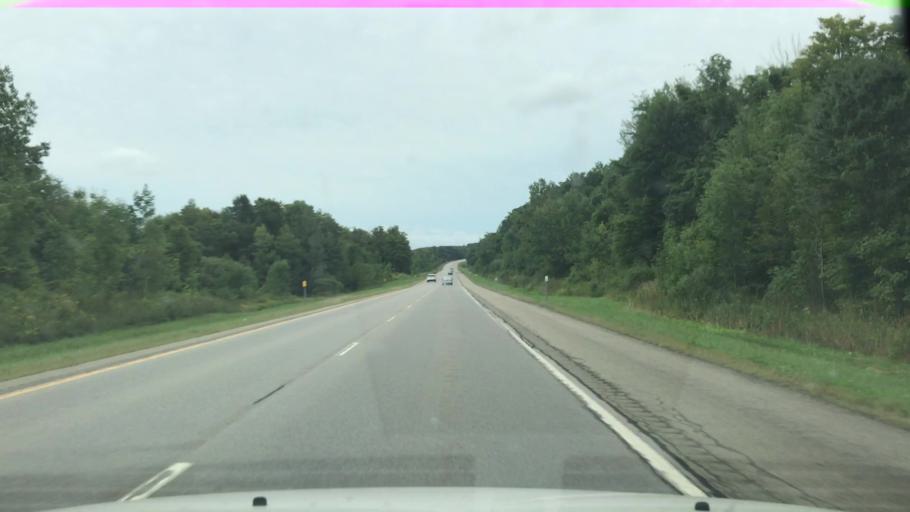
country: US
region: New York
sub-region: Erie County
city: Springville
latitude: 42.5804
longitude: -78.7260
